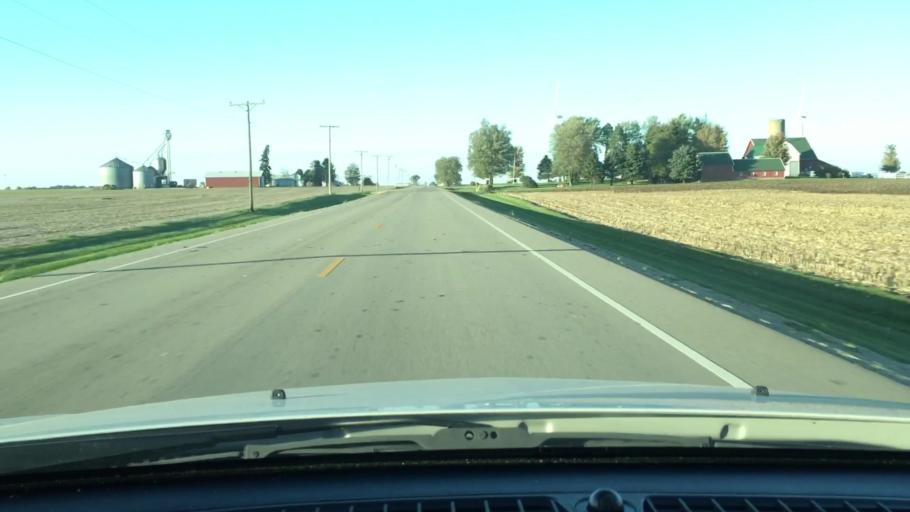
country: US
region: Illinois
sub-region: DeKalb County
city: Malta
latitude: 41.8346
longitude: -88.8864
